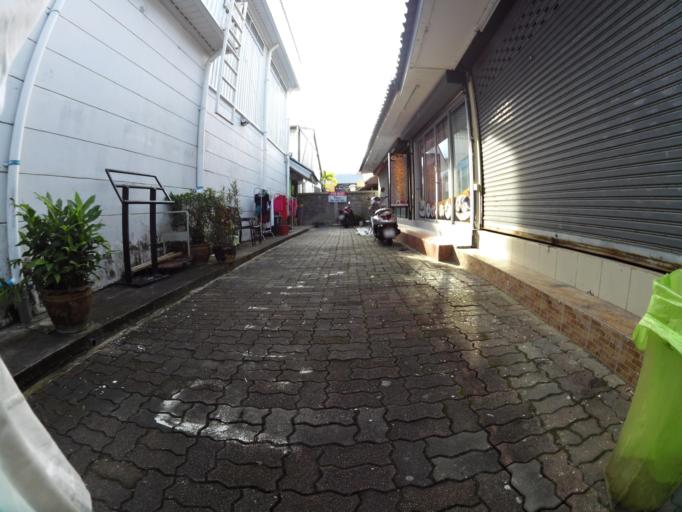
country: TH
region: Phuket
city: Patong
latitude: 7.9496
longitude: 98.2802
